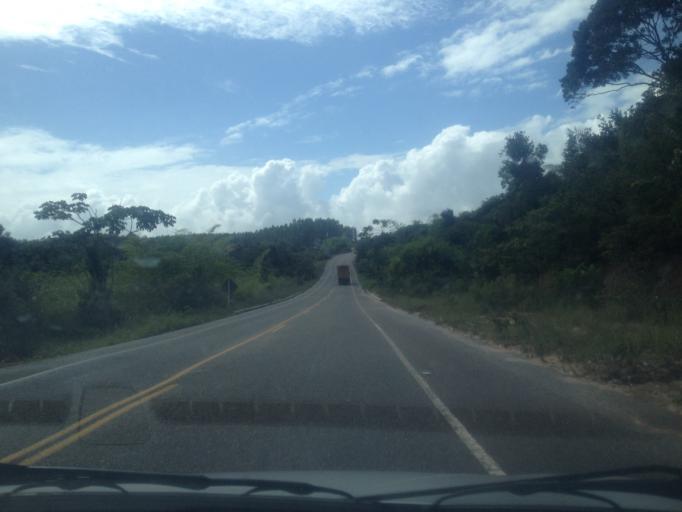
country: BR
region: Bahia
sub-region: Conde
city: Conde
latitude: -11.6699
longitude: -37.5601
